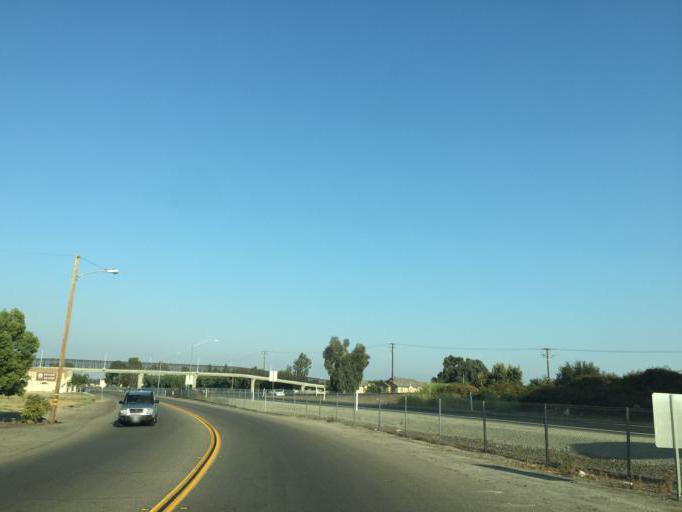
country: US
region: California
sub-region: Tulare County
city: Visalia
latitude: 36.3279
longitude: -119.2586
